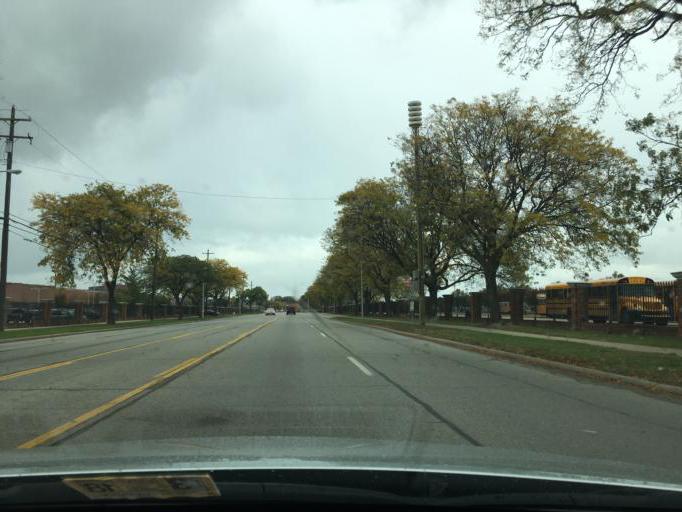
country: US
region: Michigan
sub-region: Wayne County
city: Allen Park
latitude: 42.3005
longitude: -83.2339
